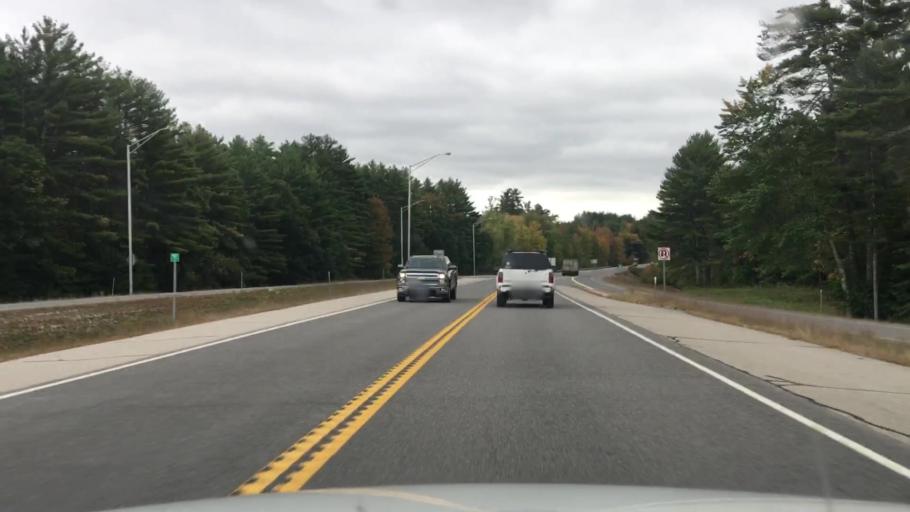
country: US
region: New Hampshire
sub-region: Carroll County
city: Ossipee
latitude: 43.7553
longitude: -71.1394
